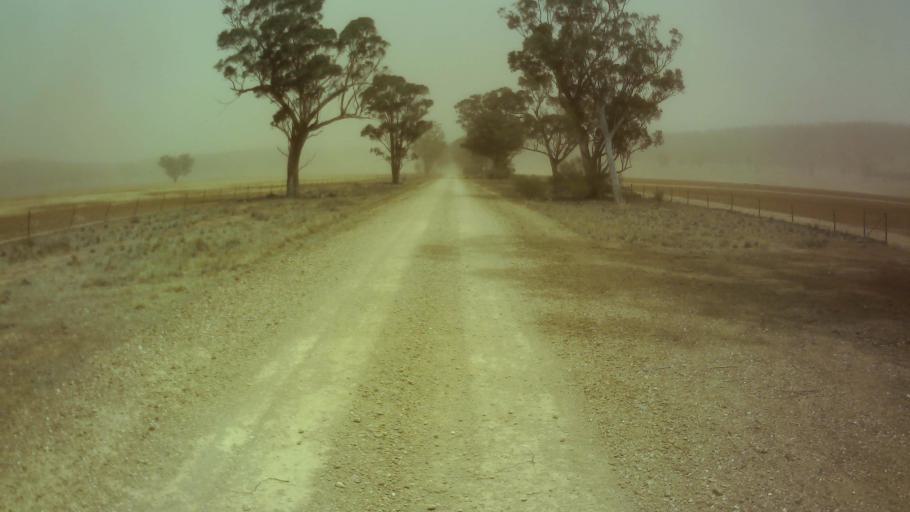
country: AU
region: New South Wales
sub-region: Weddin
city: Grenfell
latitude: -33.7114
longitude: 147.9634
